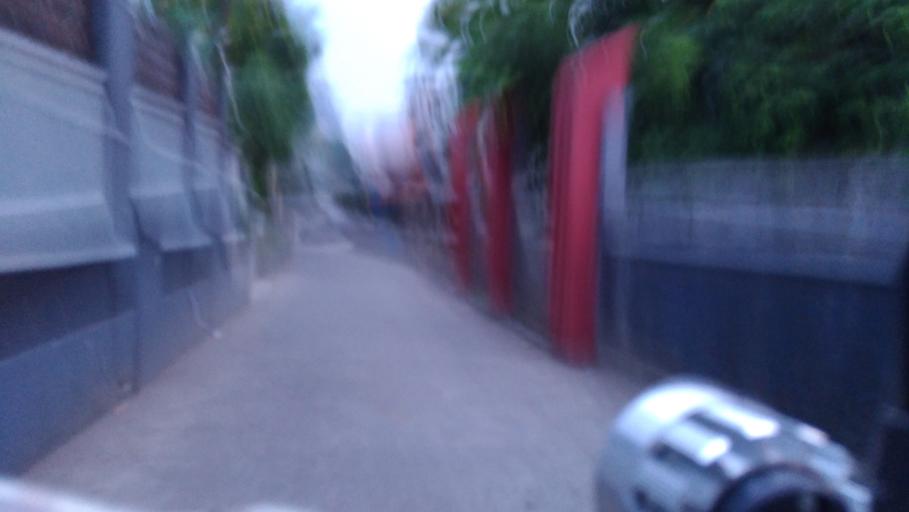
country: ID
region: West Java
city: Depok
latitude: -6.3514
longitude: 106.8701
